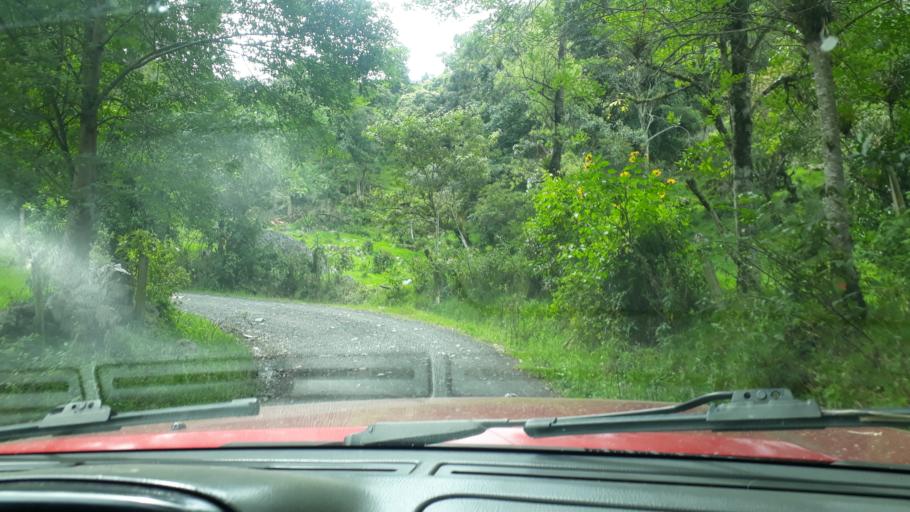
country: CO
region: Boyaca
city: San Mateo
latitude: 6.3968
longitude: -72.5419
